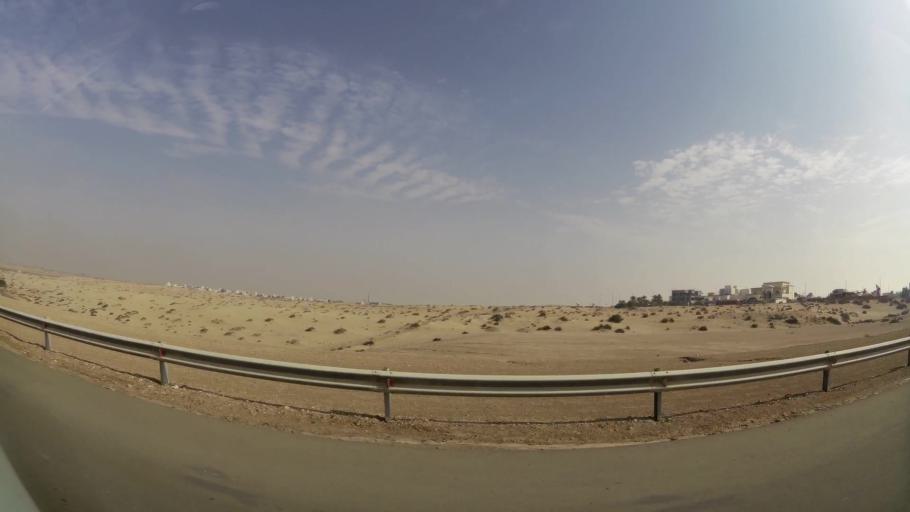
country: AE
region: Abu Dhabi
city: Abu Dhabi
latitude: 24.2652
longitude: 54.6871
